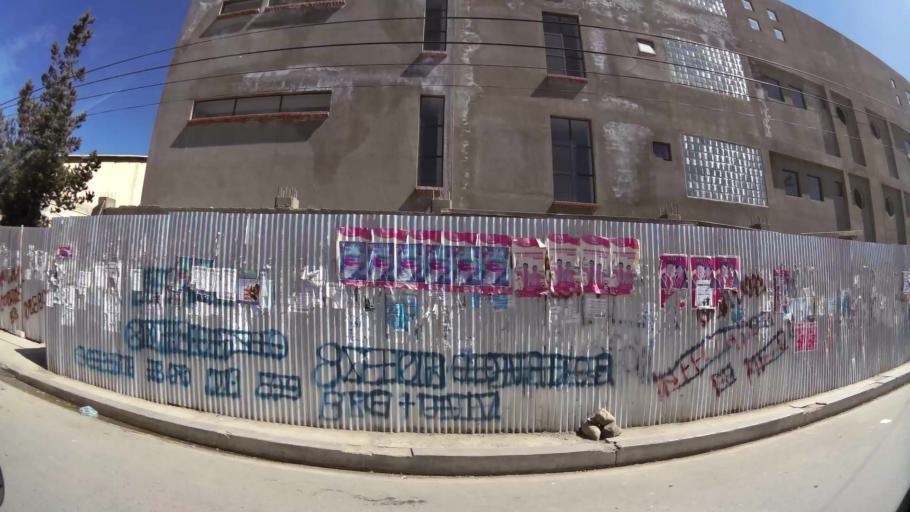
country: BO
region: La Paz
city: La Paz
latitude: -16.4900
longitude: -68.1927
